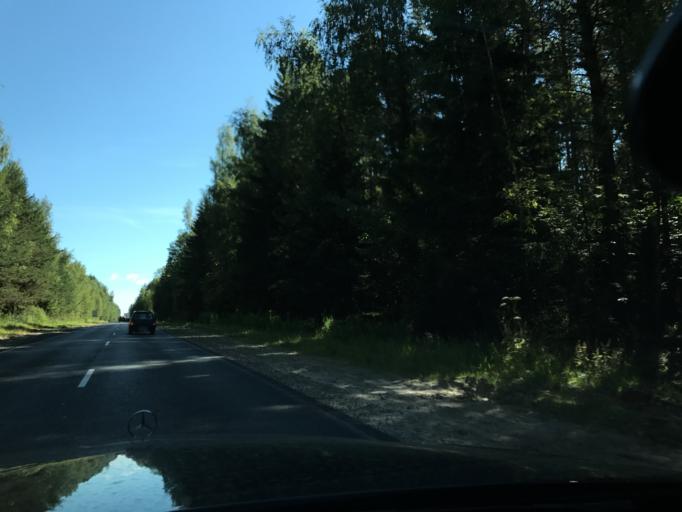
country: RU
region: Vladimir
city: Kol'chugino
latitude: 56.2883
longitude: 39.3143
